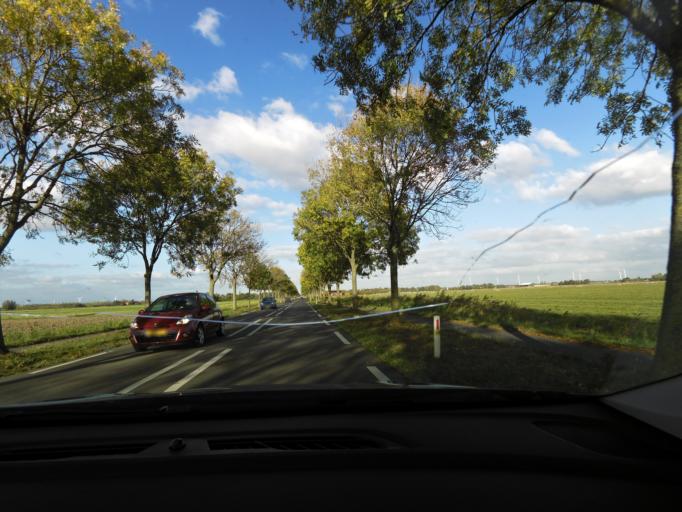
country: NL
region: North Brabant
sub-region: Gemeente Steenbergen
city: Dinteloord
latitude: 51.6221
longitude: 4.3590
